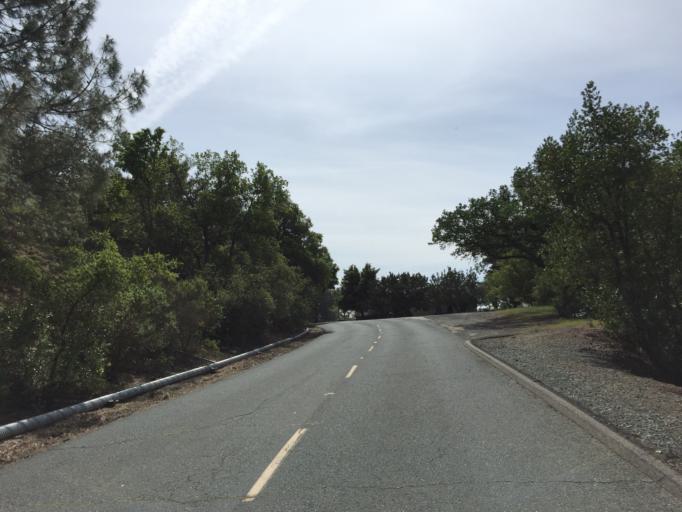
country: US
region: California
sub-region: Contra Costa County
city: Diablo
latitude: 37.8697
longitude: -121.9354
